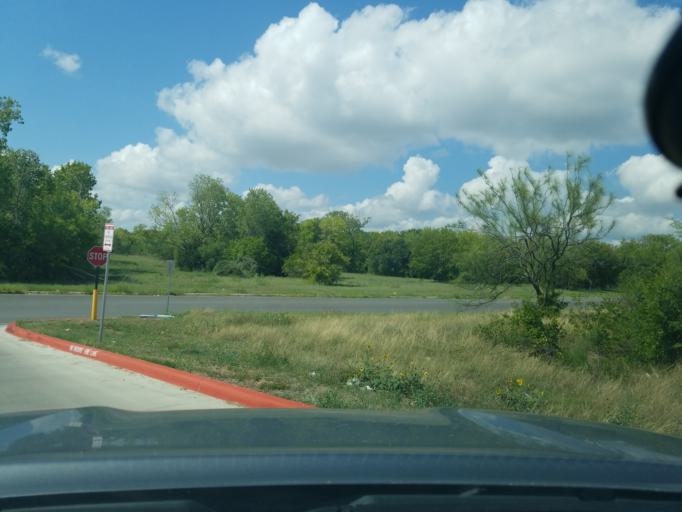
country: US
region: Texas
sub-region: Bexar County
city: San Antonio
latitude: 29.3525
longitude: -98.5392
